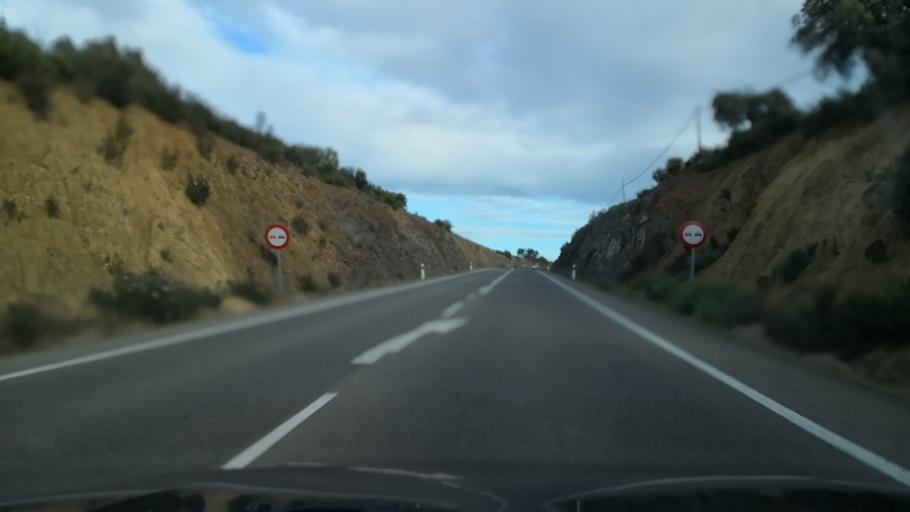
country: ES
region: Extremadura
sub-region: Provincia de Caceres
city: Pedroso de Acim
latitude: 39.8264
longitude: -6.3761
